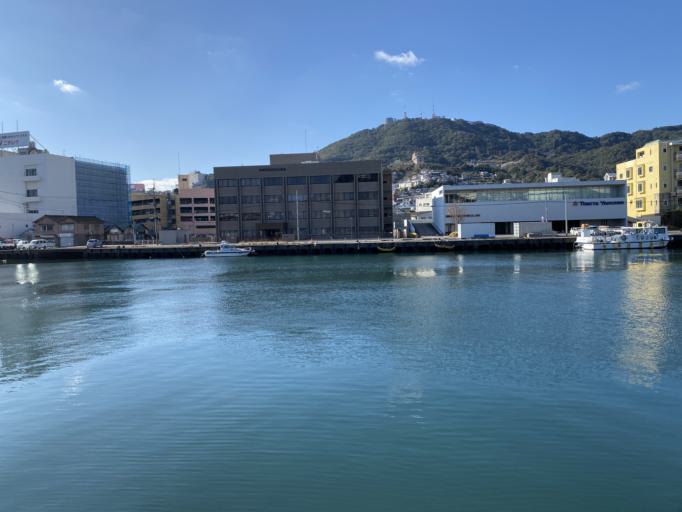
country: JP
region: Nagasaki
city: Nagasaki-shi
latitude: 32.7545
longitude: 129.8667
